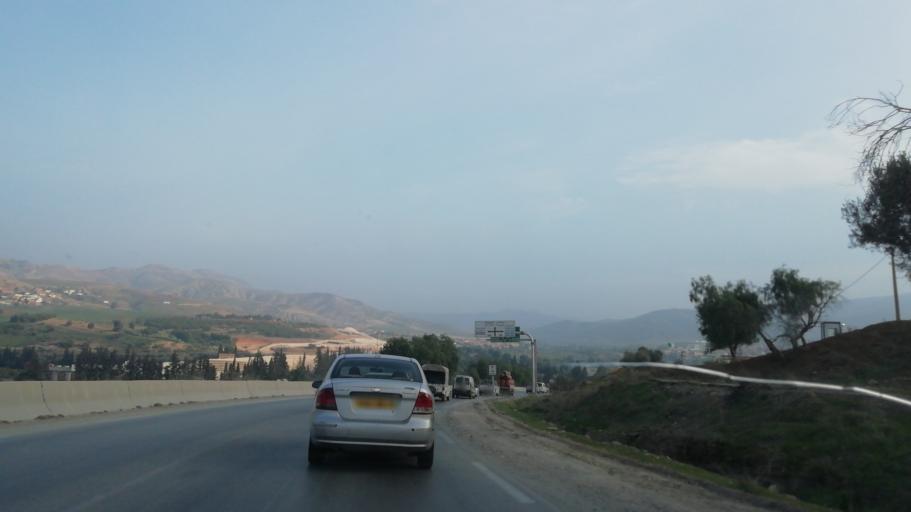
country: DZ
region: Mascara
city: Bou Hanifia el Hamamat
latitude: 35.4710
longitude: -0.0129
